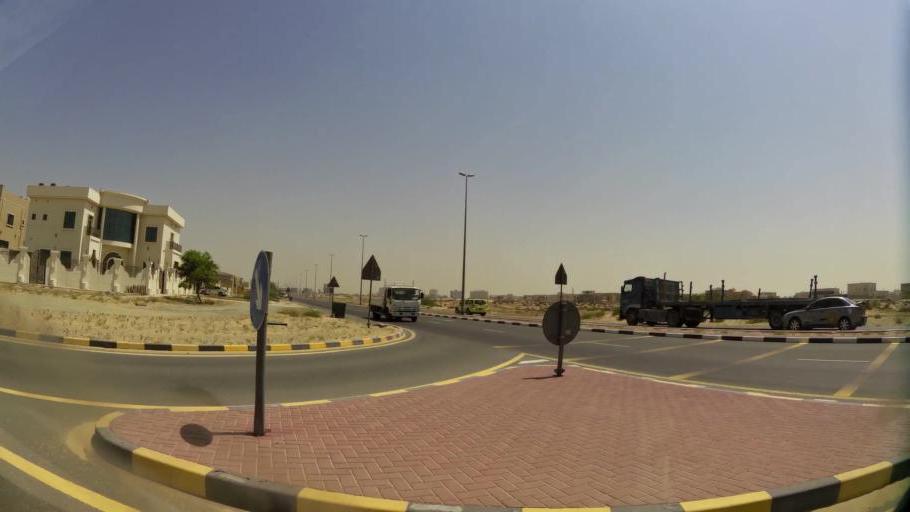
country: AE
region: Ajman
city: Ajman
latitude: 25.4142
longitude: 55.5278
